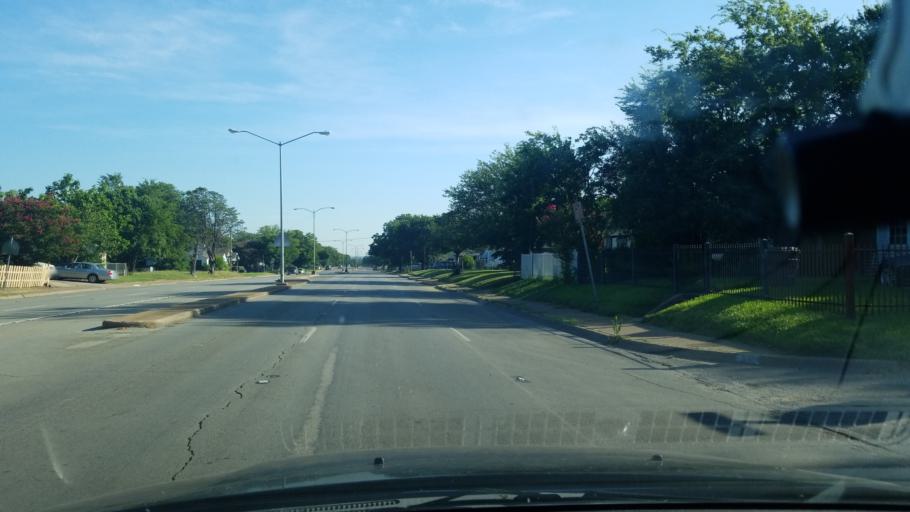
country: US
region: Texas
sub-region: Dallas County
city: Dallas
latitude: 32.7239
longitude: -96.8144
